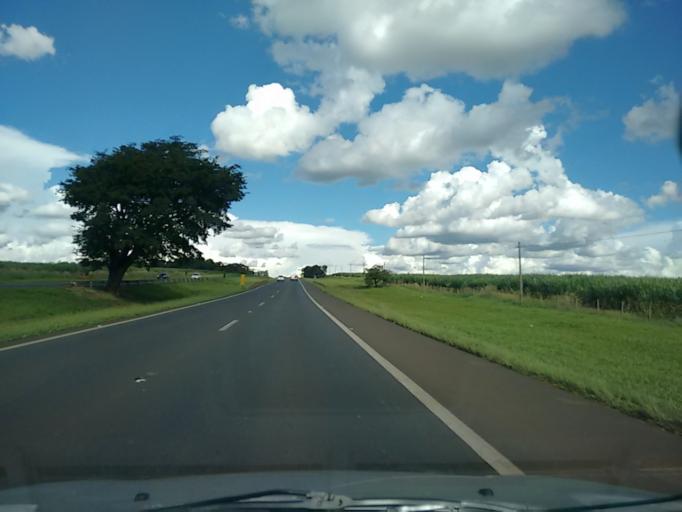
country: BR
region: Sao Paulo
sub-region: Ibate
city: Ibate
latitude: -21.9685
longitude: -47.9582
